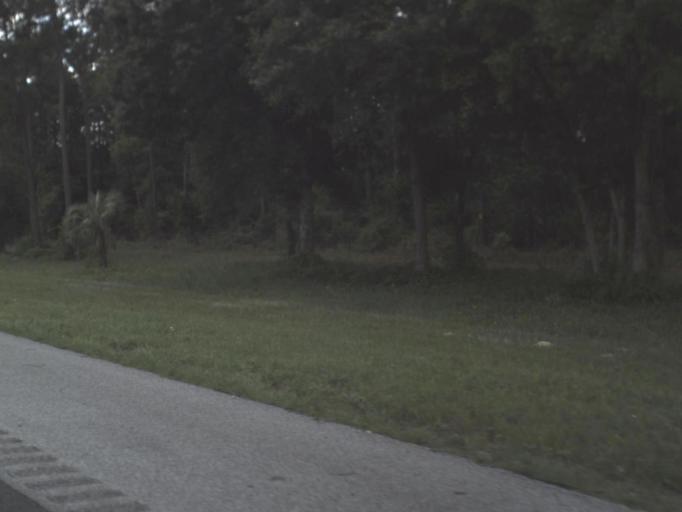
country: US
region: Florida
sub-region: Suwannee County
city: Wellborn
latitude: 30.3342
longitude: -82.8233
